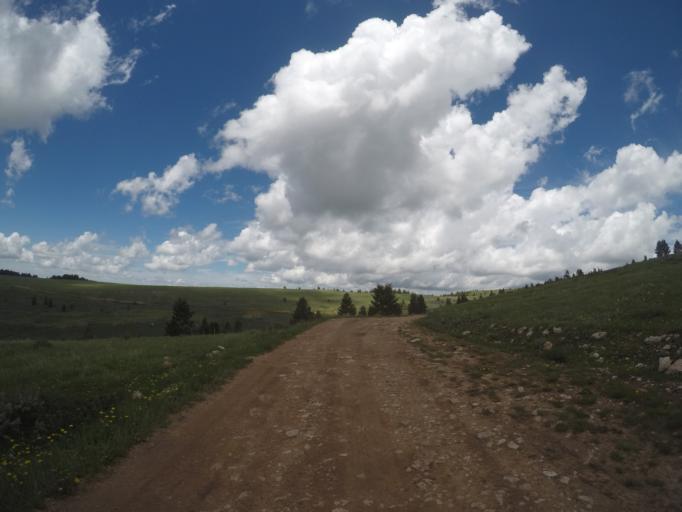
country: US
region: Wyoming
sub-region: Big Horn County
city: Lovell
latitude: 45.1771
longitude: -108.4378
